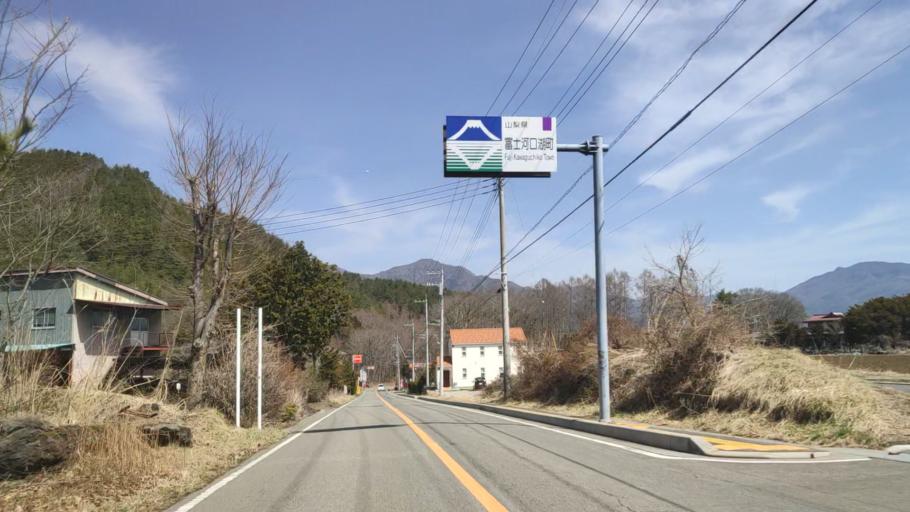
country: JP
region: Yamanashi
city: Fujikawaguchiko
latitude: 35.4906
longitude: 138.7279
